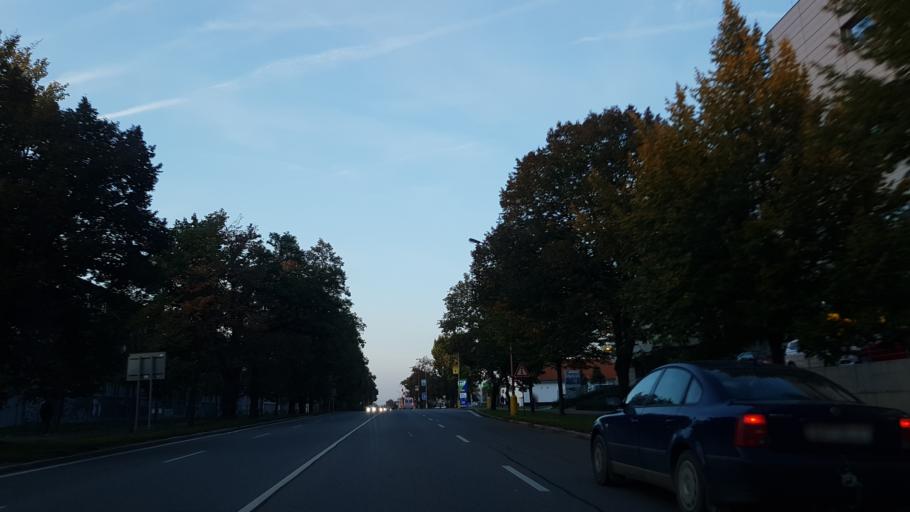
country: CZ
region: Zlin
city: Kunovice
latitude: 49.0547
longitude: 17.4666
